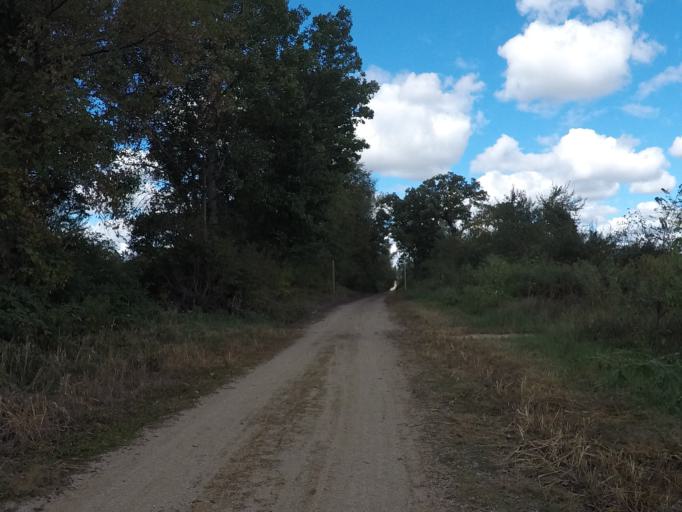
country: US
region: Wisconsin
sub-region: Richland County
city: Richland Center
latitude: 43.3049
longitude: -90.3403
